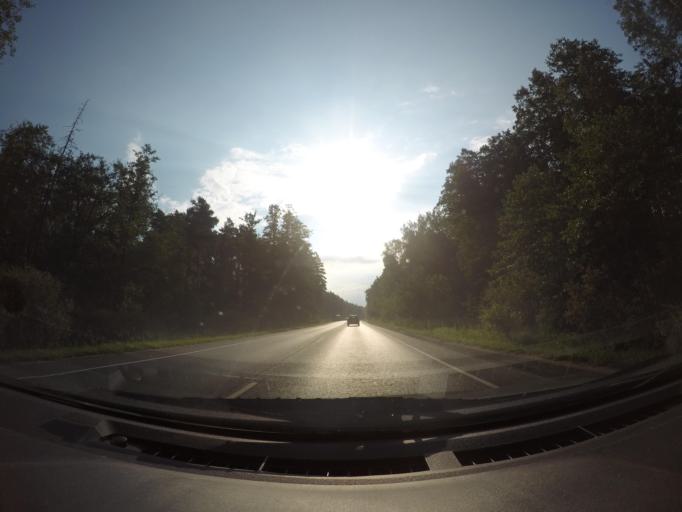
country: RU
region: Moskovskaya
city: Ramenskoye
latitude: 55.6387
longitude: 38.2443
